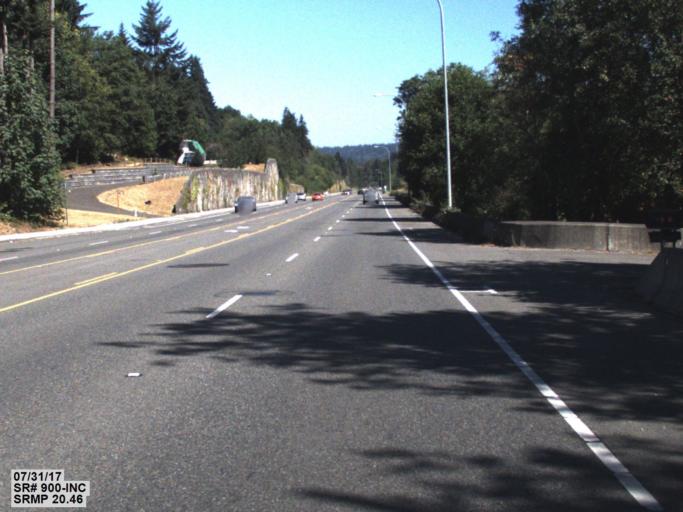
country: US
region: Washington
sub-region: King County
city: Issaquah
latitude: 47.5322
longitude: -122.0621
